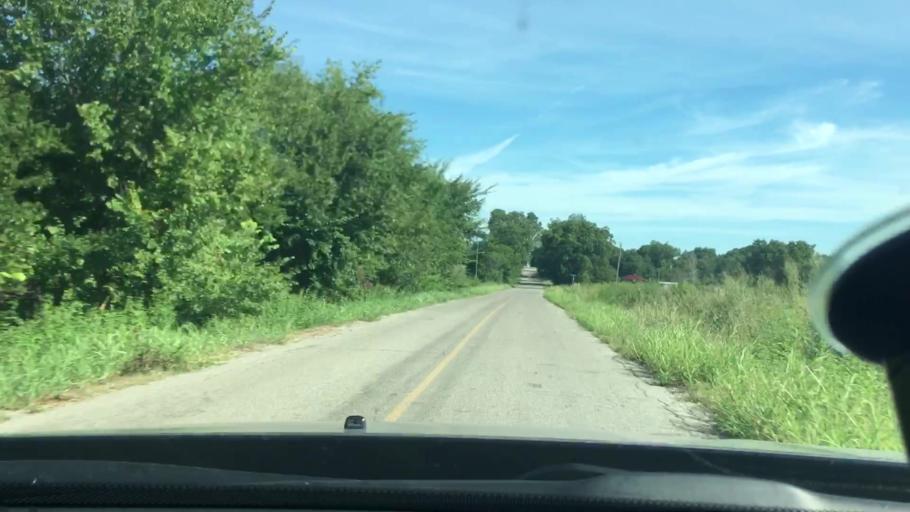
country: US
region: Oklahoma
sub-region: Carter County
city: Lone Grove
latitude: 34.2879
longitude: -97.2825
